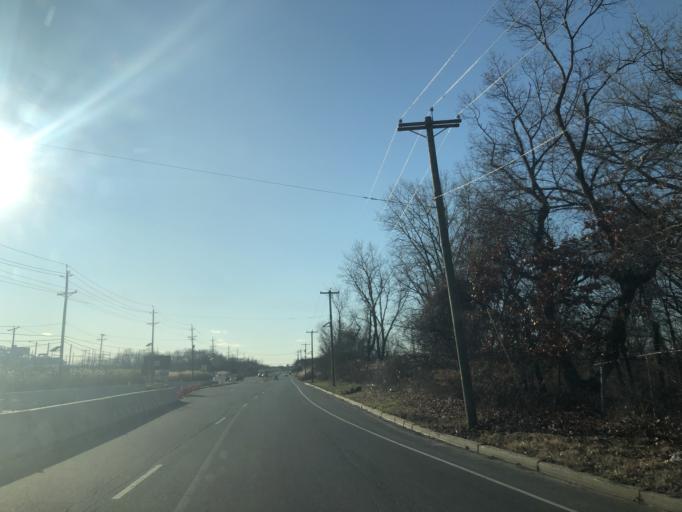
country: US
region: New Jersey
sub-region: Middlesex County
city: Fords
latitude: 40.5199
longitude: -74.3146
